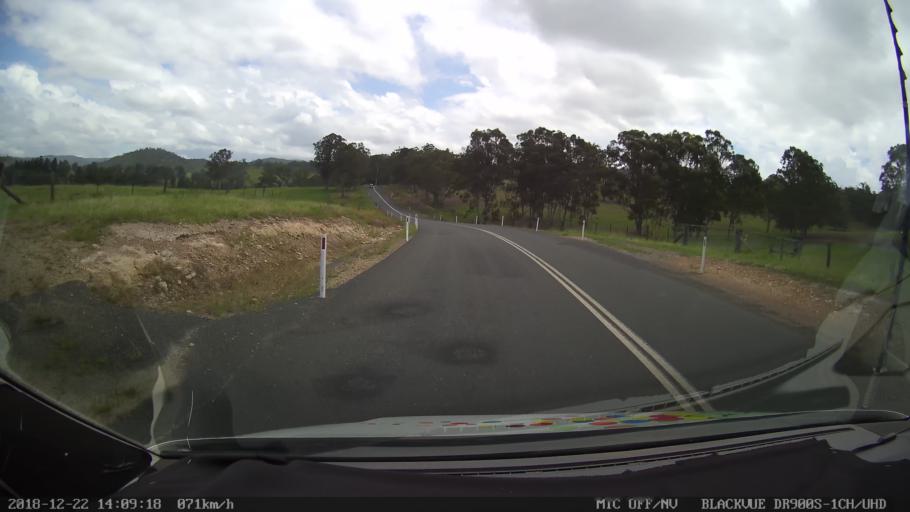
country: AU
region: New South Wales
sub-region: Clarence Valley
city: Coutts Crossing
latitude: -29.9853
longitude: 152.7184
